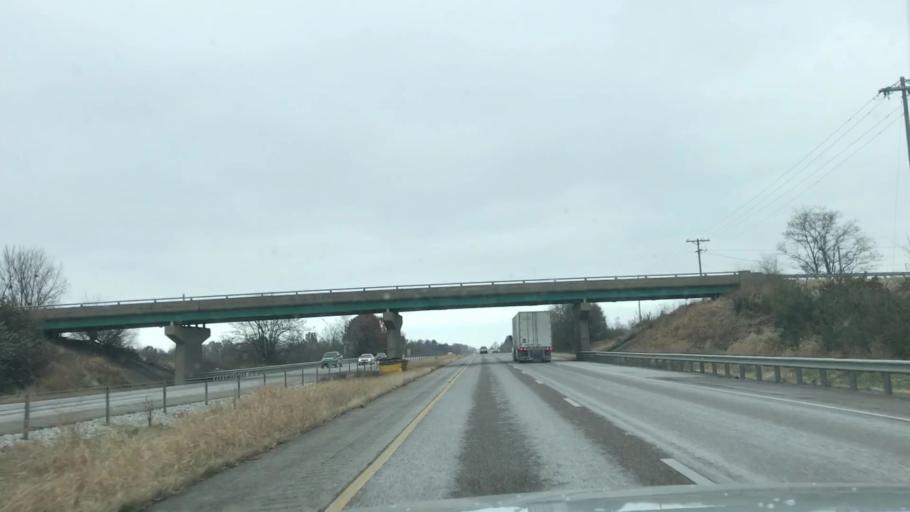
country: US
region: Illinois
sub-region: Madison County
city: Troy
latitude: 38.7586
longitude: -89.9053
